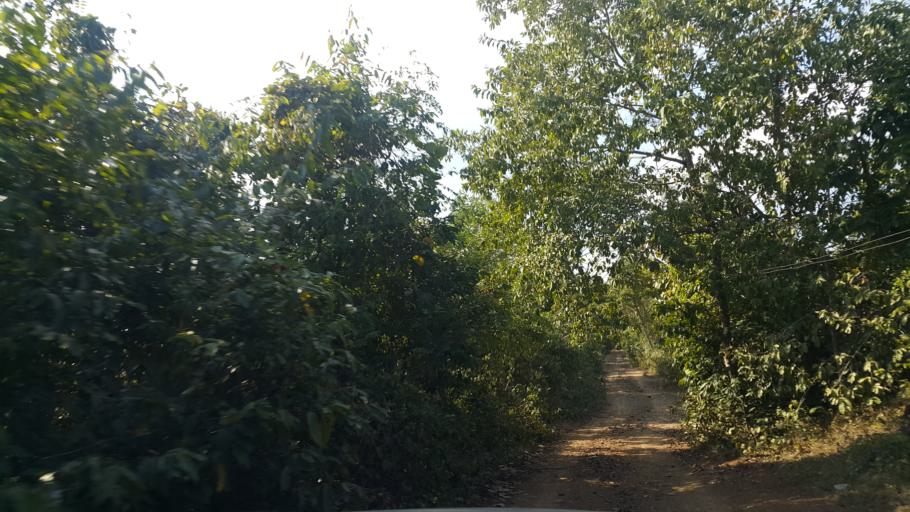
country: TH
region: Lamphun
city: Ban Thi
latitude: 18.5651
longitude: 99.1220
